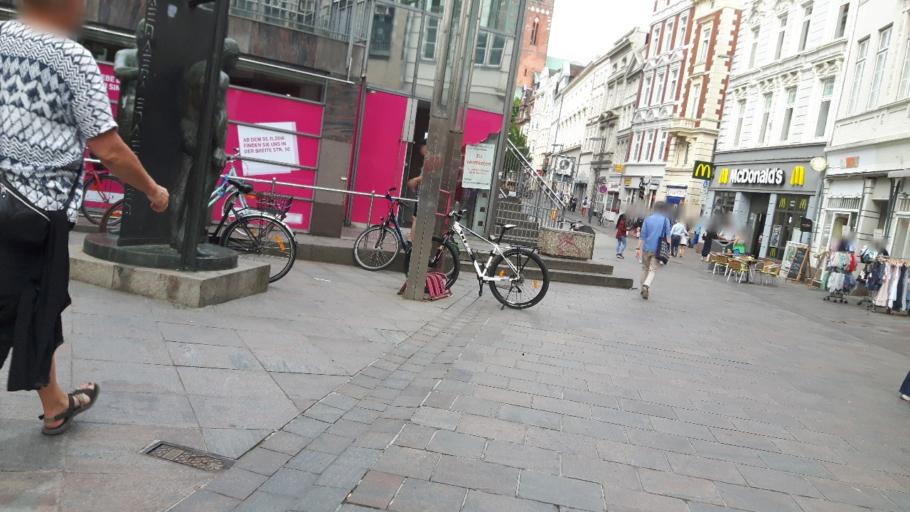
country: DE
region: Schleswig-Holstein
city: Luebeck
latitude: 53.8693
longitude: 10.6873
